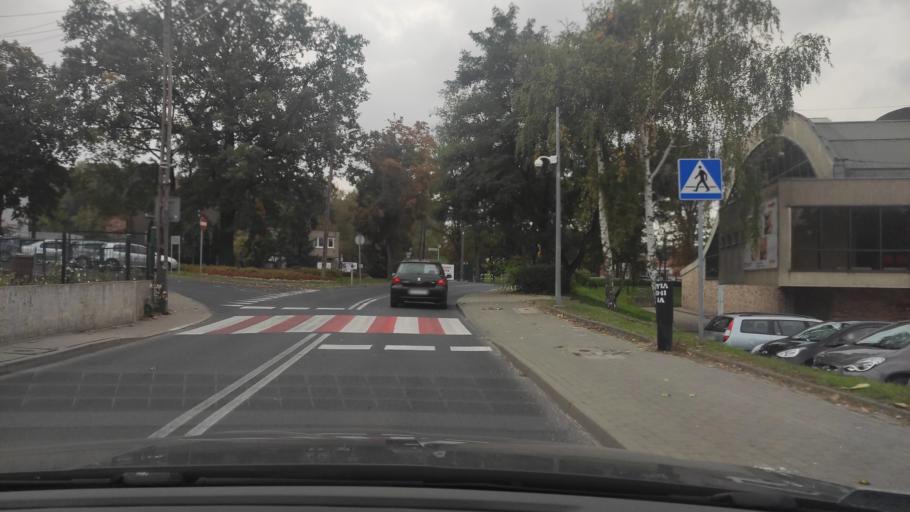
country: PL
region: Greater Poland Voivodeship
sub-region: Powiat poznanski
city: Swarzedz
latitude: 52.4104
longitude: 17.0714
